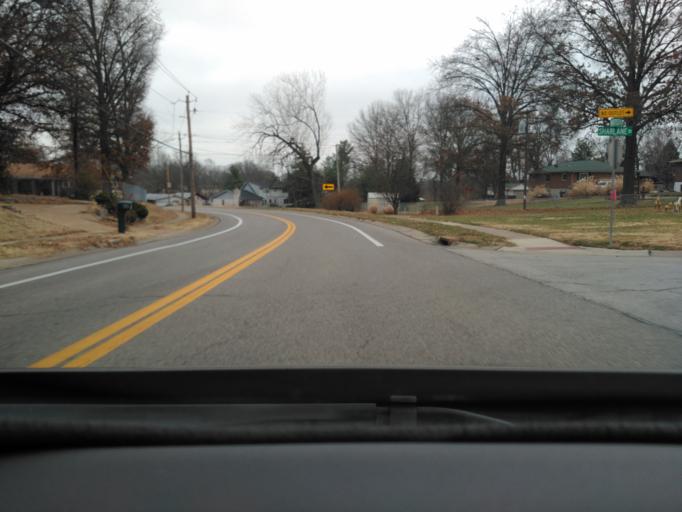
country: US
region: Missouri
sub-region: Saint Louis County
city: Concord
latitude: 38.4976
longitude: -90.3563
